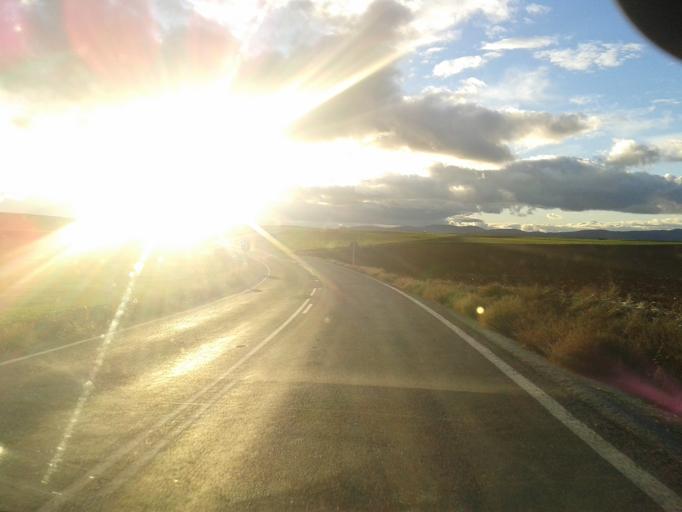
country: ES
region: Aragon
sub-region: Provincia de Teruel
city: Ferreruela de Huerva
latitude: 41.0618
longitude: -1.2404
